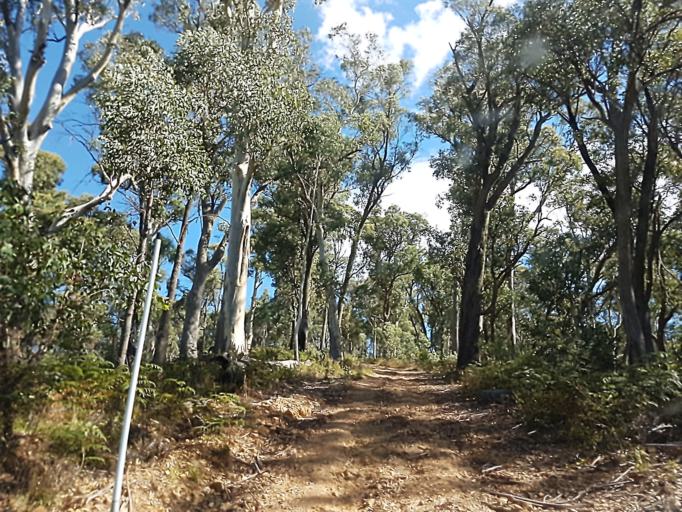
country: AU
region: Victoria
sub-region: Alpine
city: Mount Beauty
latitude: -36.8813
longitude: 147.0245
